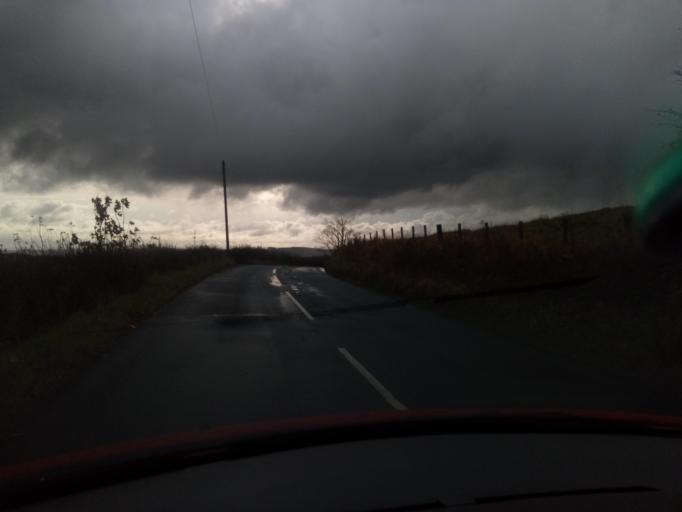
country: GB
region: England
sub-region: Northumberland
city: Birtley
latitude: 55.1229
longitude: -2.2303
